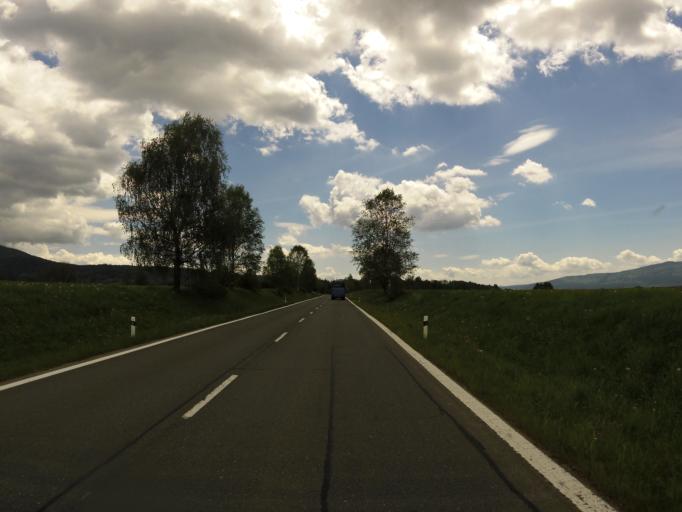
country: CZ
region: Jihocesky
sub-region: Okres Prachatice
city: Volary
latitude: 48.8374
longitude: 13.9490
